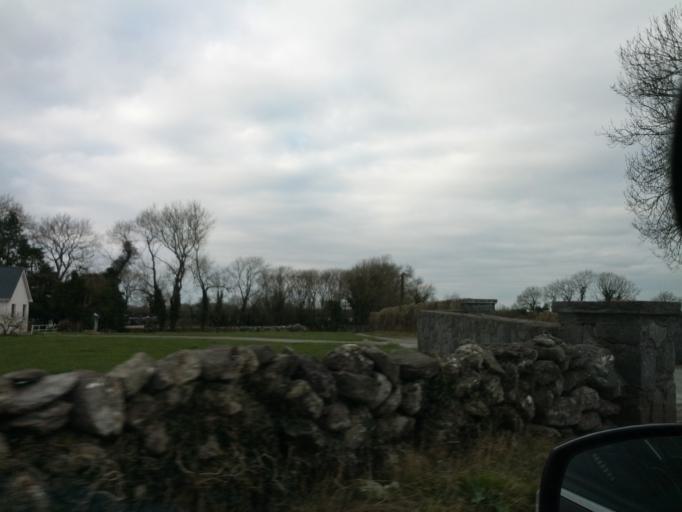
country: IE
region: Connaught
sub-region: County Galway
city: Gort
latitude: 53.1731
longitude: -8.8483
